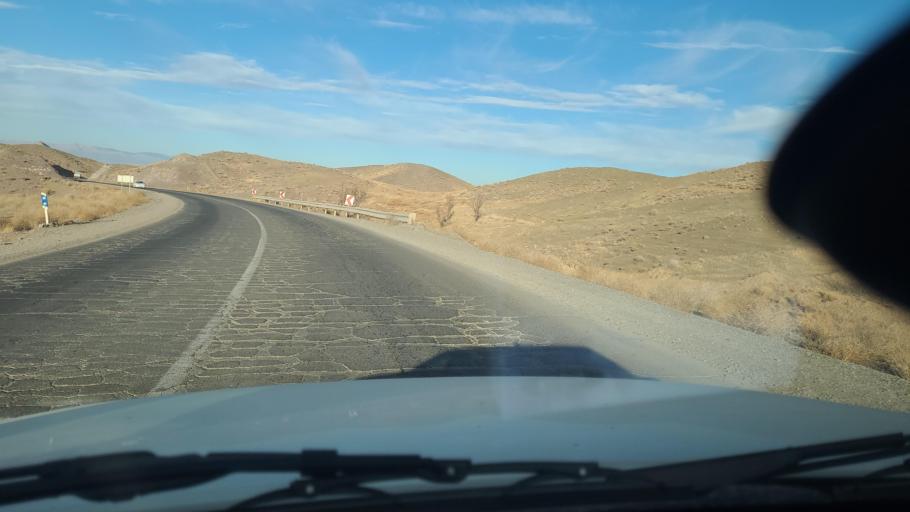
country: IR
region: Razavi Khorasan
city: Sabzevar
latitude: 36.4113
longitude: 57.5505
